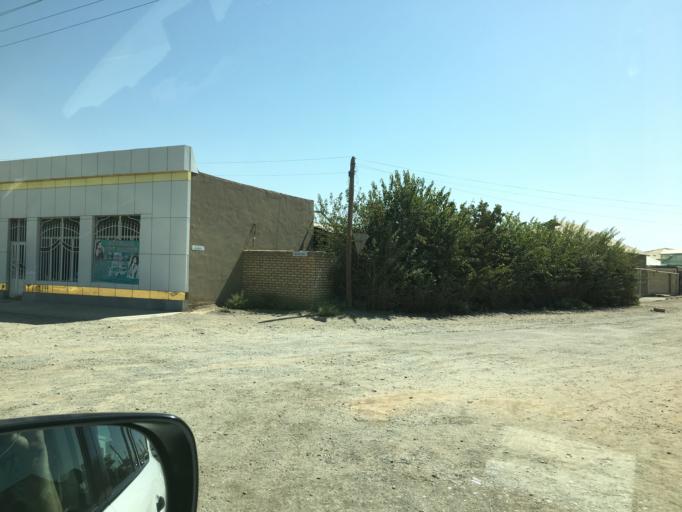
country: IR
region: Razavi Khorasan
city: Sarakhs
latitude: 36.5321
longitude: 61.2175
